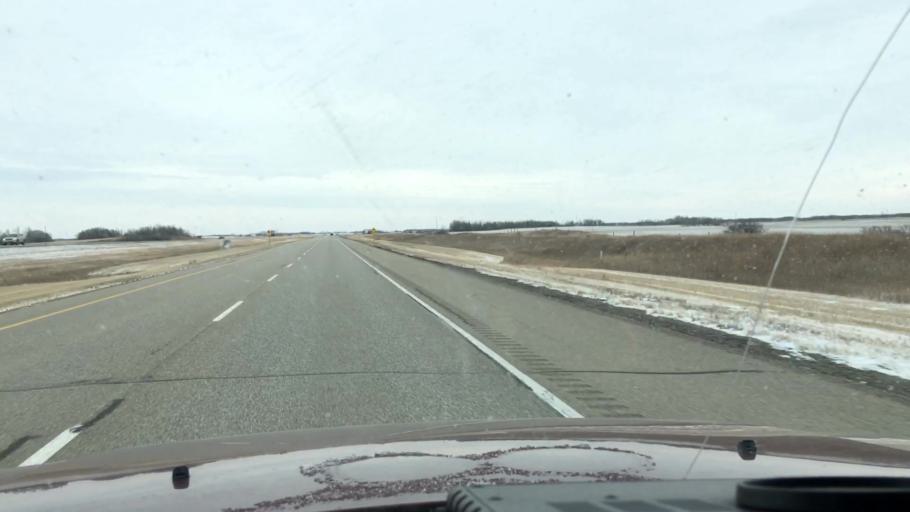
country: CA
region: Saskatchewan
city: Watrous
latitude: 51.3381
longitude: -106.0928
